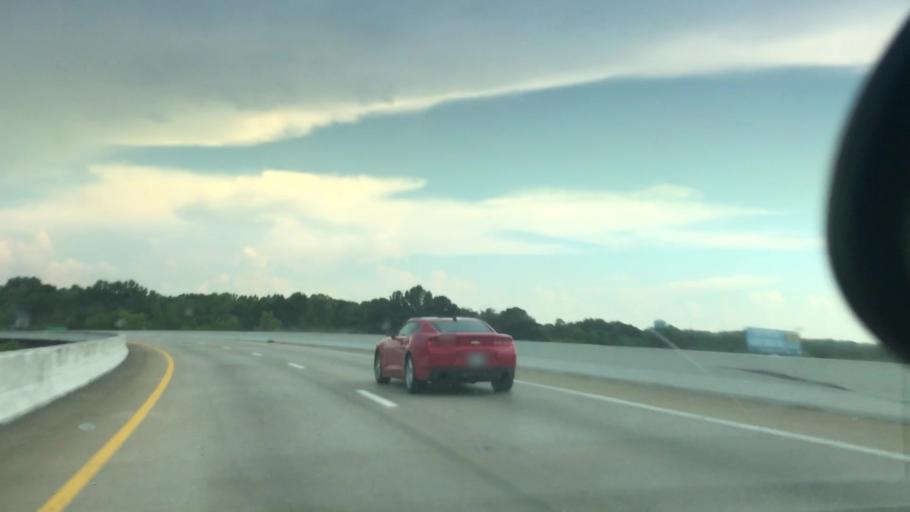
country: US
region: Tennessee
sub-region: Shelby County
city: Bartlett
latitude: 35.1511
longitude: -89.8833
